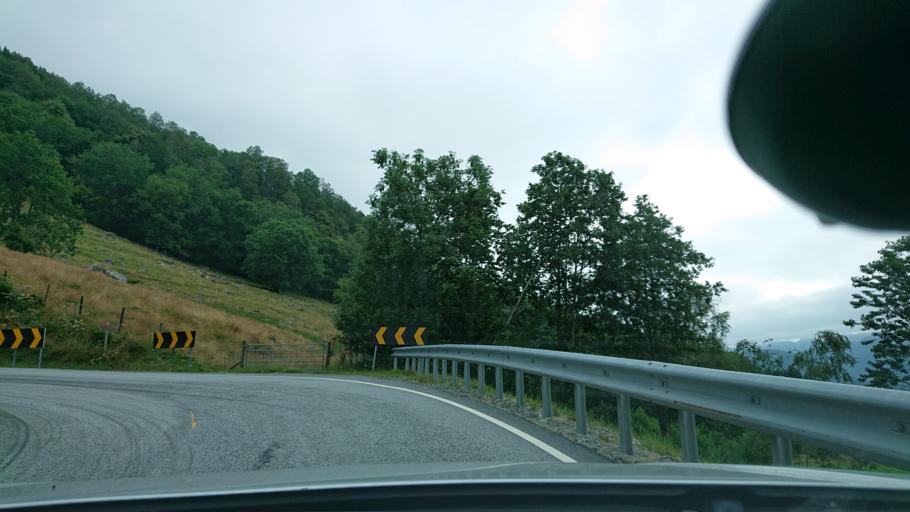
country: NO
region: Rogaland
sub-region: Hjelmeland
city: Hjelmelandsvagen
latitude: 59.1683
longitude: 6.1718
